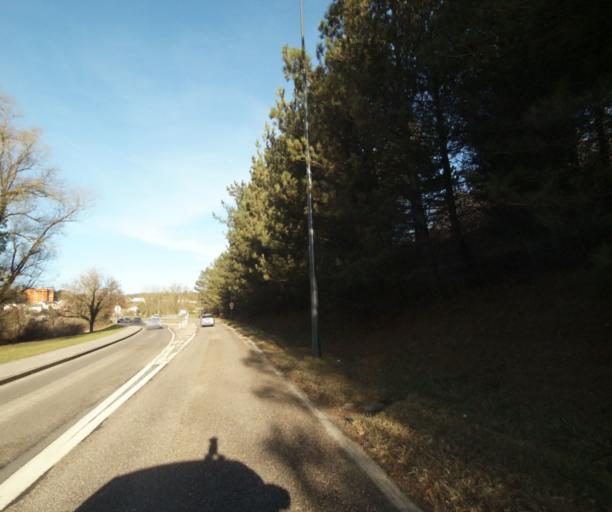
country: FR
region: Lorraine
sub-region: Departement de Meurthe-et-Moselle
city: Chavigny
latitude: 48.6580
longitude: 6.1195
